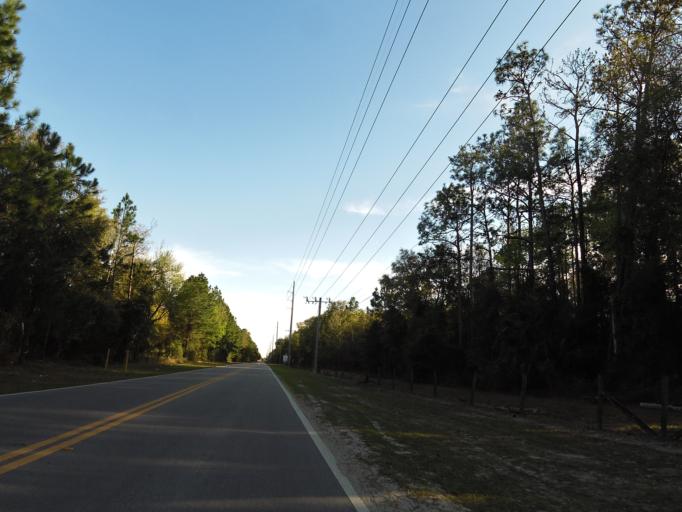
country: US
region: Florida
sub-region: Duval County
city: Jacksonville
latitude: 30.4385
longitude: -81.6047
